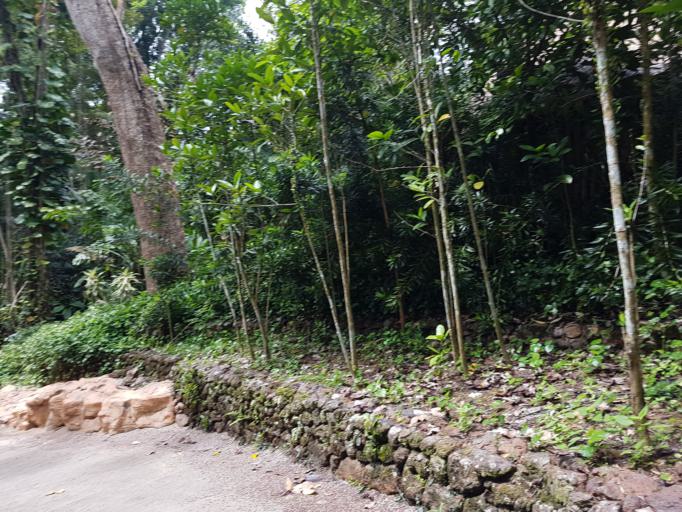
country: MY
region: Johor
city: Johor Bahru
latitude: 1.4058
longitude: 103.7940
